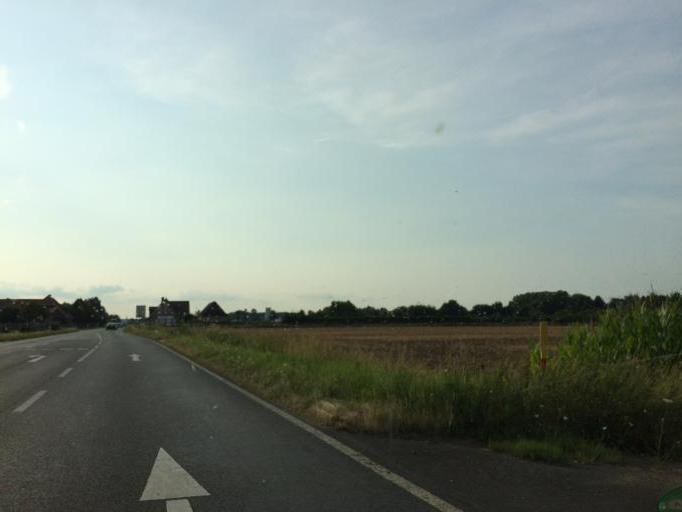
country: DE
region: North Rhine-Westphalia
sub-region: Regierungsbezirk Munster
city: Nottuln
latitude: 51.9146
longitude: 7.3885
